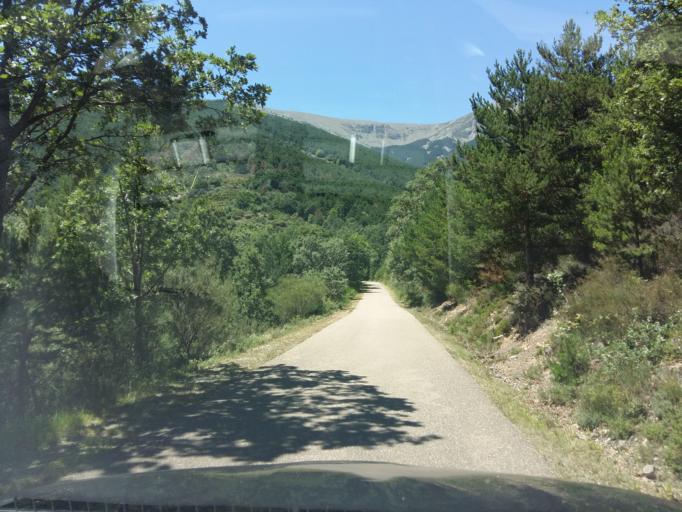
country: ES
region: Aragon
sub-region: Provincia de Zaragoza
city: Litago
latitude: 41.7869
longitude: -1.7717
